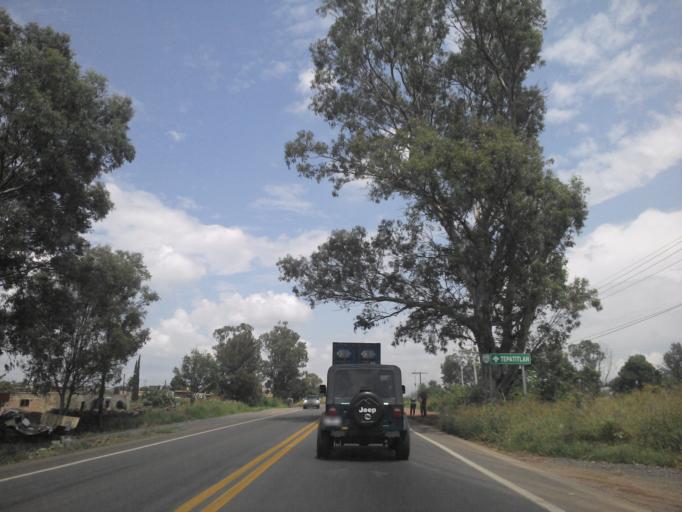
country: MX
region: Jalisco
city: Zapotlanejo
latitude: 20.6834
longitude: -102.9984
